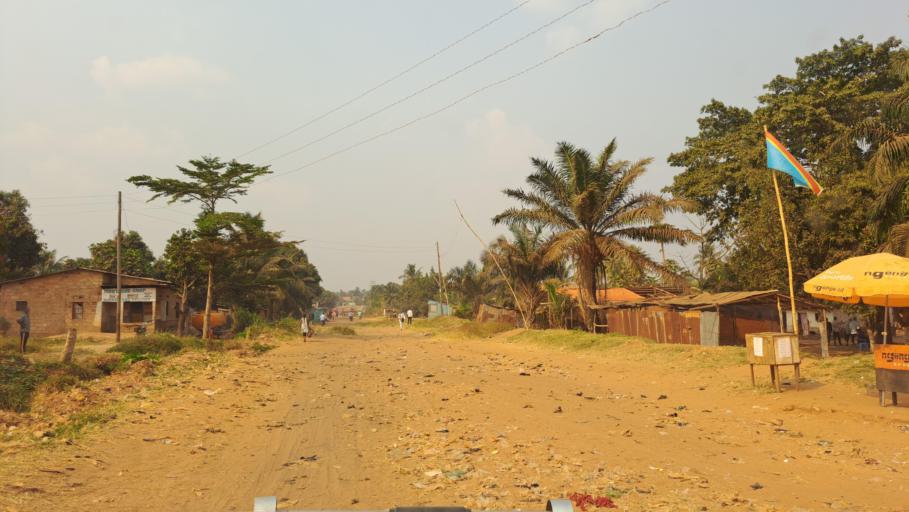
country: CD
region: Kasai-Oriental
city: Mbuji-Mayi
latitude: -6.1243
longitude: 23.6029
